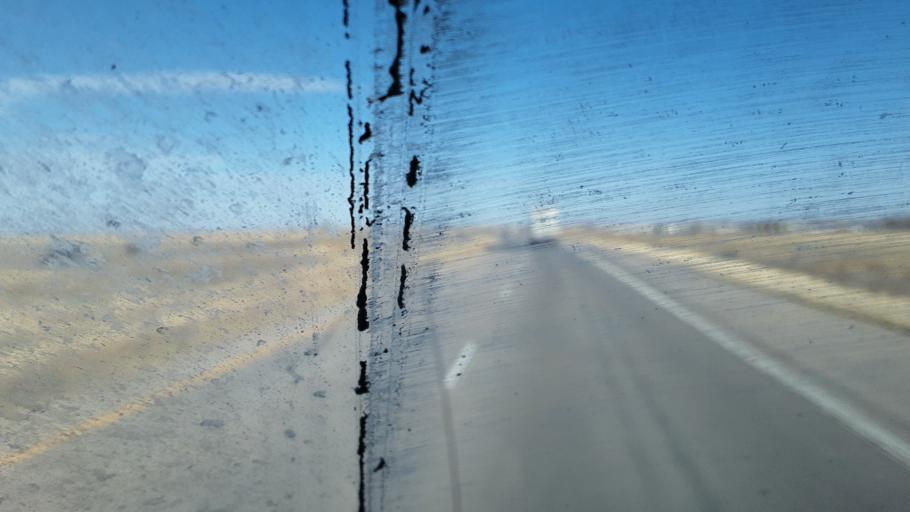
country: US
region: Colorado
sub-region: Weld County
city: Keenesburg
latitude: 40.1193
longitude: -104.5061
